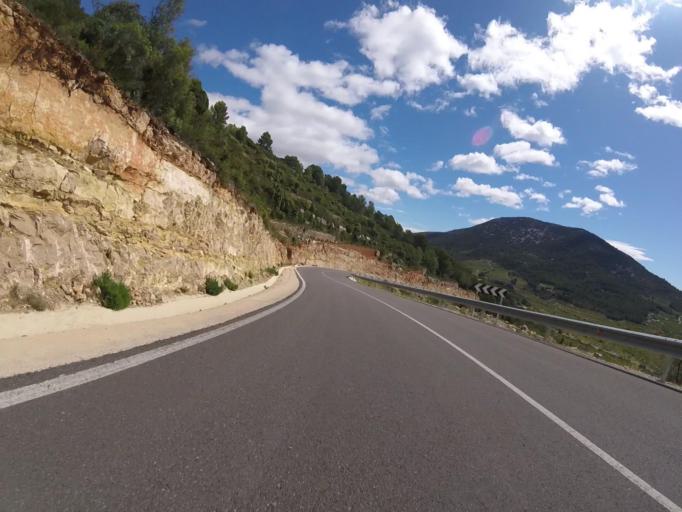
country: ES
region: Valencia
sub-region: Provincia de Castello
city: Culla
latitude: 40.2937
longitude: -0.1176
